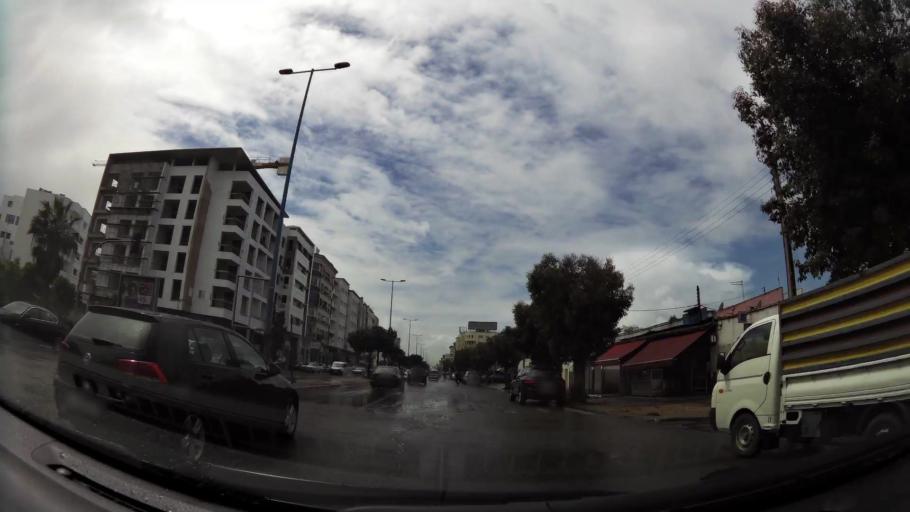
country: MA
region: Grand Casablanca
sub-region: Casablanca
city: Casablanca
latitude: 33.5763
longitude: -7.6388
